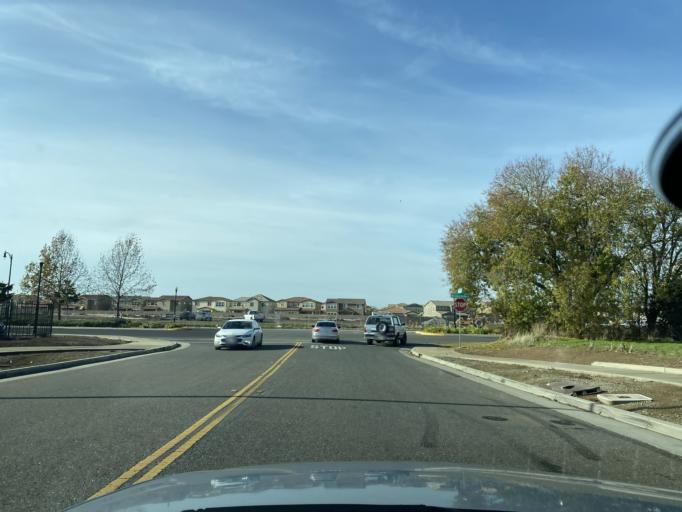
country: US
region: California
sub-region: Sacramento County
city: Elk Grove
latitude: 38.4040
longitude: -121.3943
